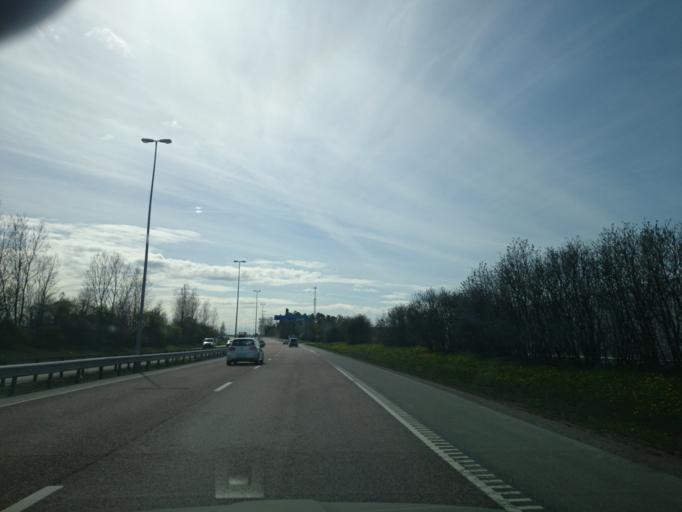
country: SE
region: Uppsala
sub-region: Uppsala Kommun
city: Gamla Uppsala
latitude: 59.8748
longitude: 17.6044
